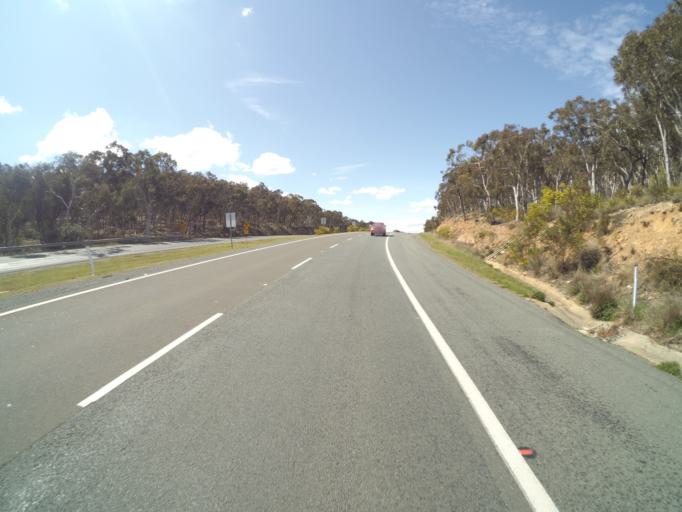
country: AU
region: New South Wales
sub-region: Goulburn Mulwaree
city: Goulburn
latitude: -34.7423
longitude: 149.7590
